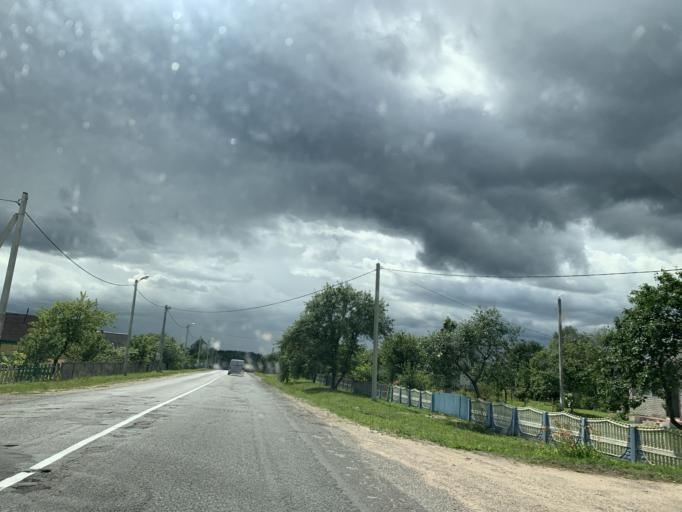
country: BY
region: Minsk
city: Ivyanyets
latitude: 53.9713
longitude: 26.8410
